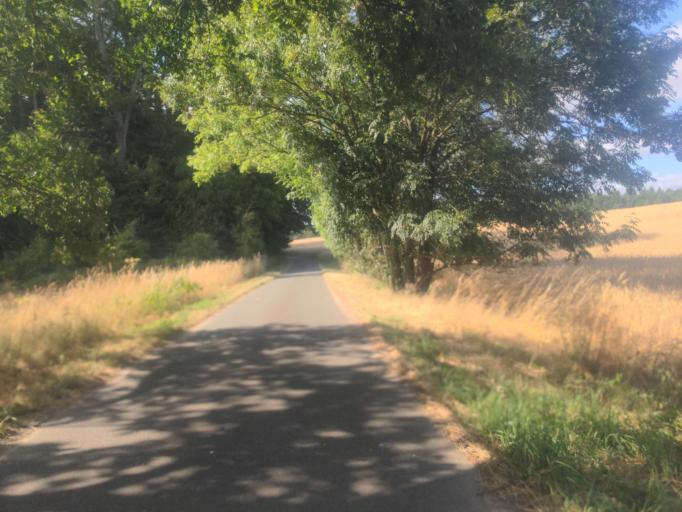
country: DE
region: Lower Saxony
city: Neu Darchau
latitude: 53.2074
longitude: 10.8624
